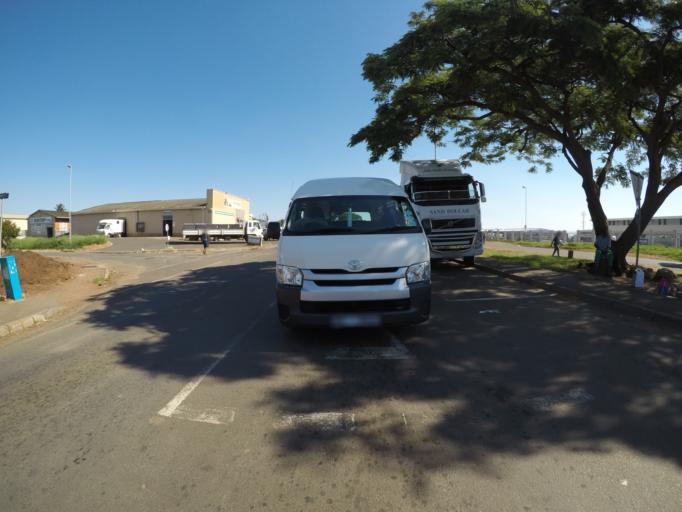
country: ZA
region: KwaZulu-Natal
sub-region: uThungulu District Municipality
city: Empangeni
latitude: -28.7774
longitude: 31.9001
